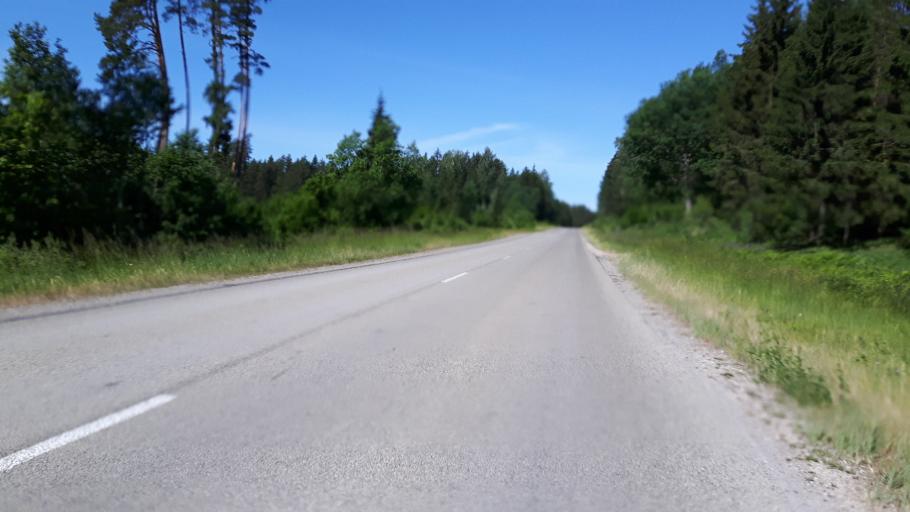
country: LV
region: Tukuma Rajons
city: Tukums
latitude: 57.0046
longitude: 23.0728
